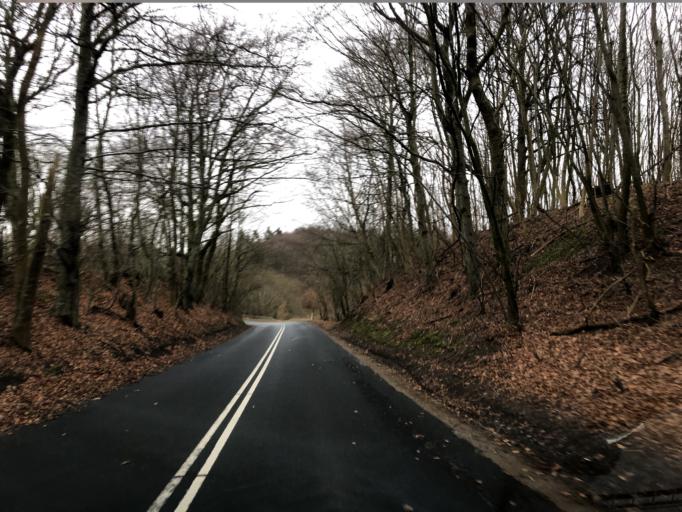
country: DK
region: Central Jutland
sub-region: Viborg Kommune
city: Stoholm
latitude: 56.4597
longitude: 9.1391
